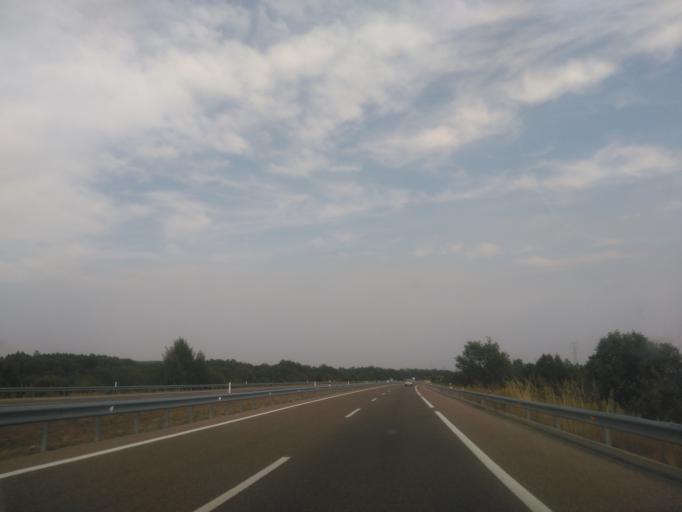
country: ES
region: Castille and Leon
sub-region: Provincia de Zamora
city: Cernadilla
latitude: 42.0375
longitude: -6.4429
